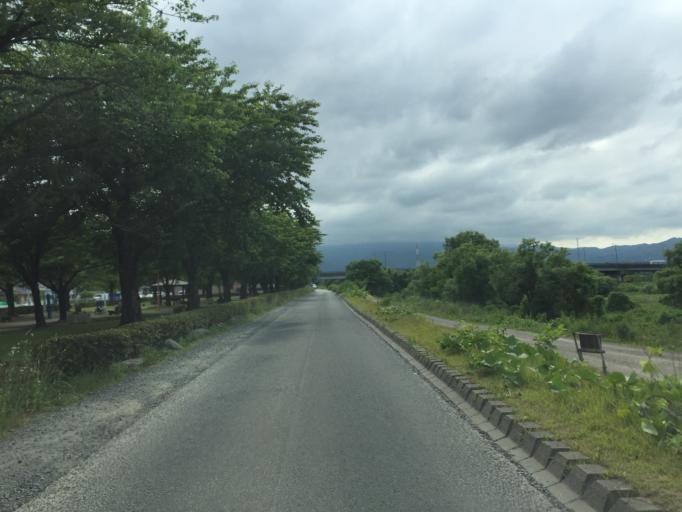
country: JP
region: Fukushima
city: Fukushima-shi
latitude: 37.7542
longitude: 140.4387
